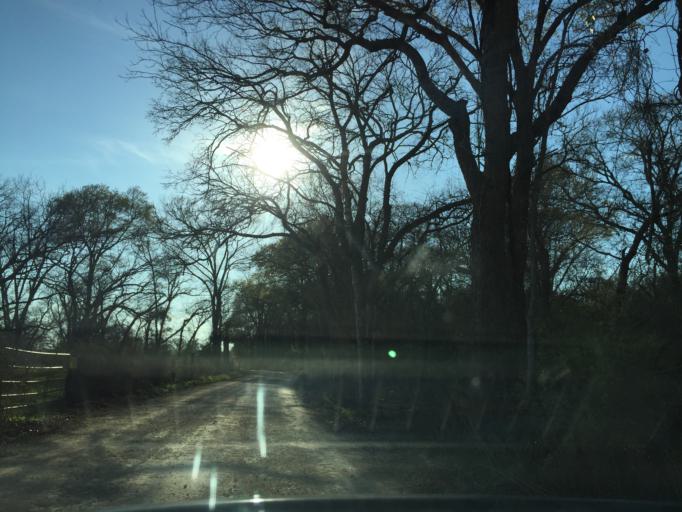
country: US
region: Texas
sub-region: Bastrop County
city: Elgin
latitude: 30.4139
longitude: -97.2216
